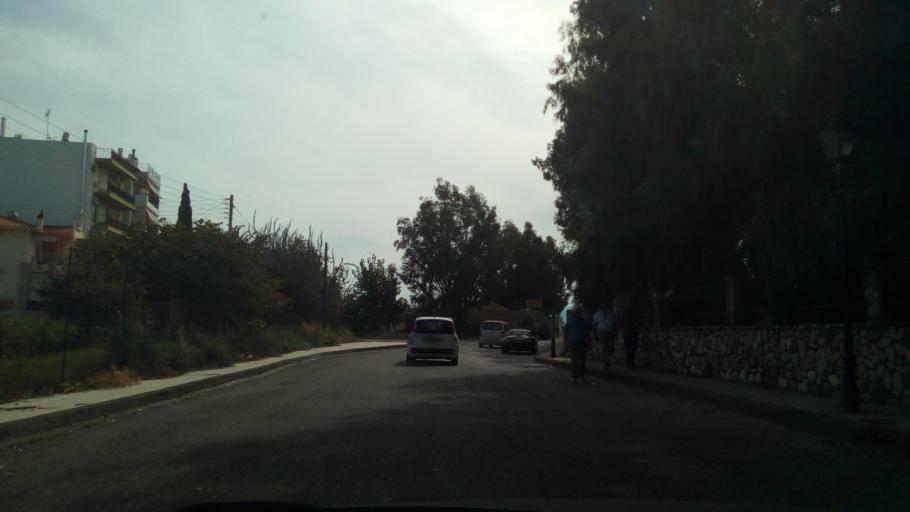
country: GR
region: West Greece
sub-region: Nomos Aitolias kai Akarnanias
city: Nafpaktos
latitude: 38.3900
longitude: 21.8410
